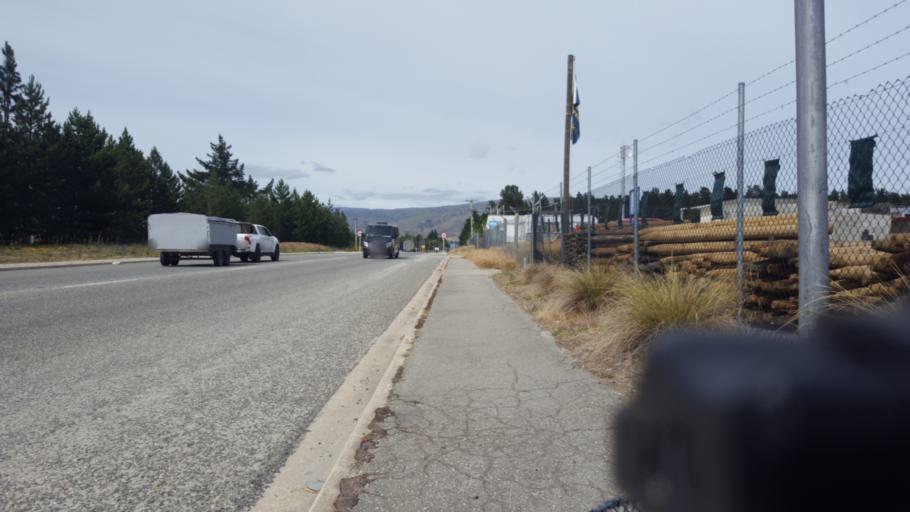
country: NZ
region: Otago
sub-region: Queenstown-Lakes District
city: Wanaka
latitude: -45.0540
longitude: 169.1942
